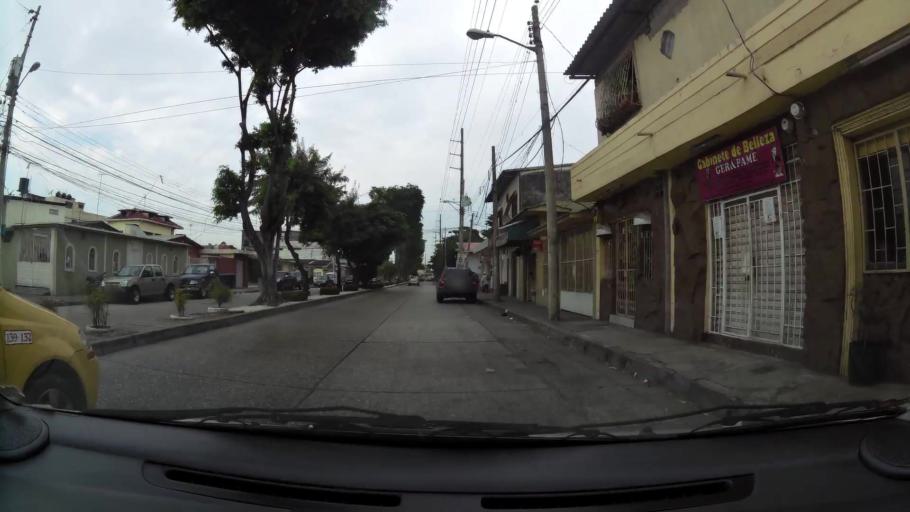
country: EC
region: Guayas
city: Guayaquil
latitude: -2.2466
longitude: -79.8971
